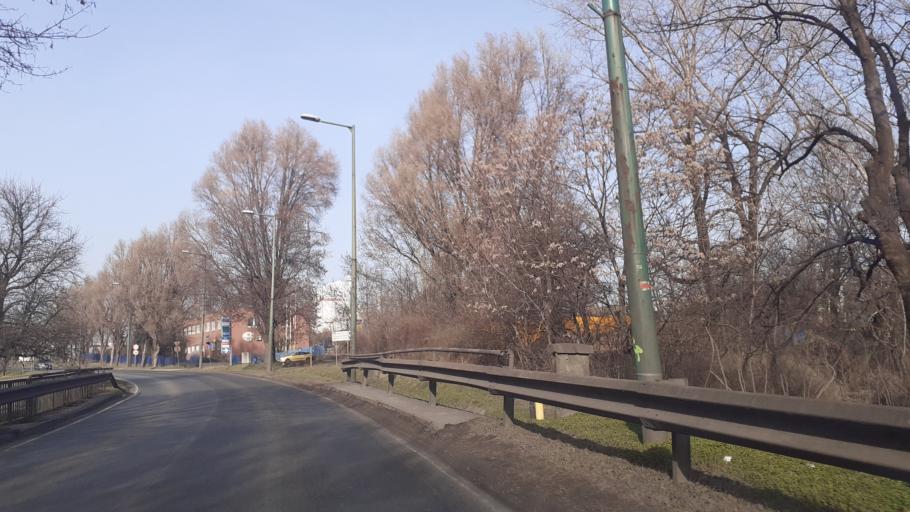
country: HU
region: Bacs-Kiskun
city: Dunavecse
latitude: 46.9344
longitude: 18.9520
